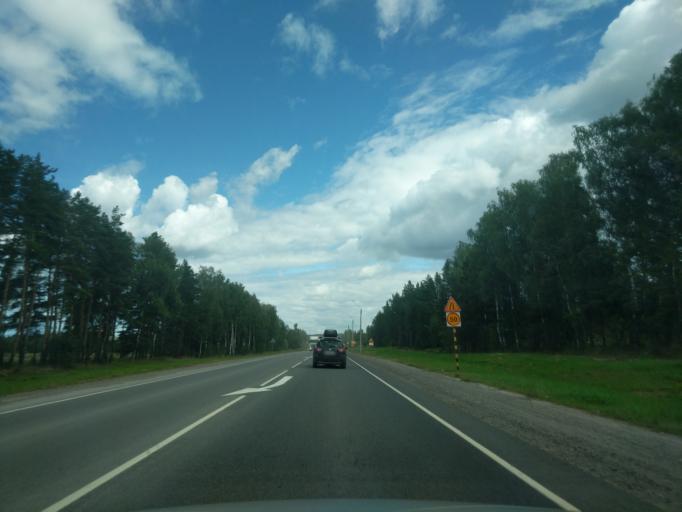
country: RU
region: Jaroslavl
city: Levashevo
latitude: 57.6478
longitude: 40.5464
